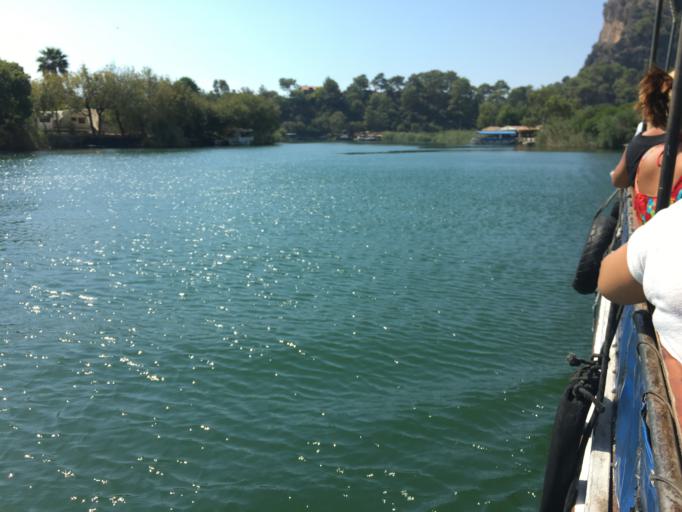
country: TR
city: Dalyan
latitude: 36.8287
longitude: 28.6326
